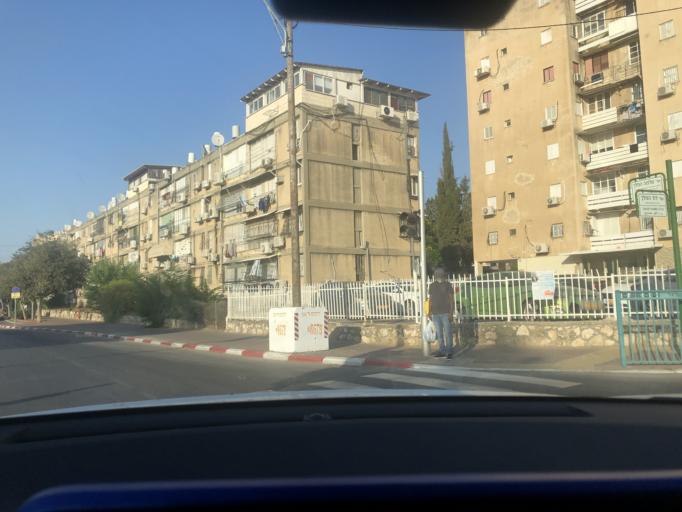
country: IL
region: Central District
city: Lod
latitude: 31.9497
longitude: 34.8882
